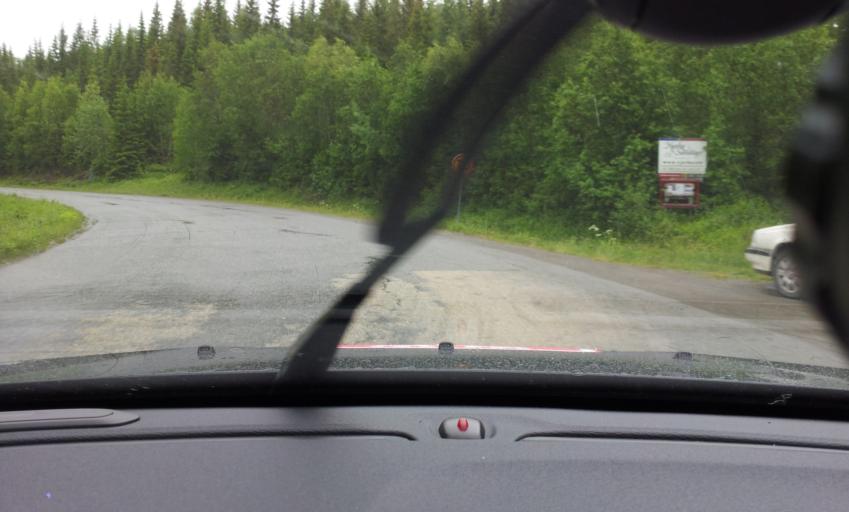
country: SE
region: Jaemtland
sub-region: Are Kommun
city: Are
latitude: 63.3987
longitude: 12.8468
